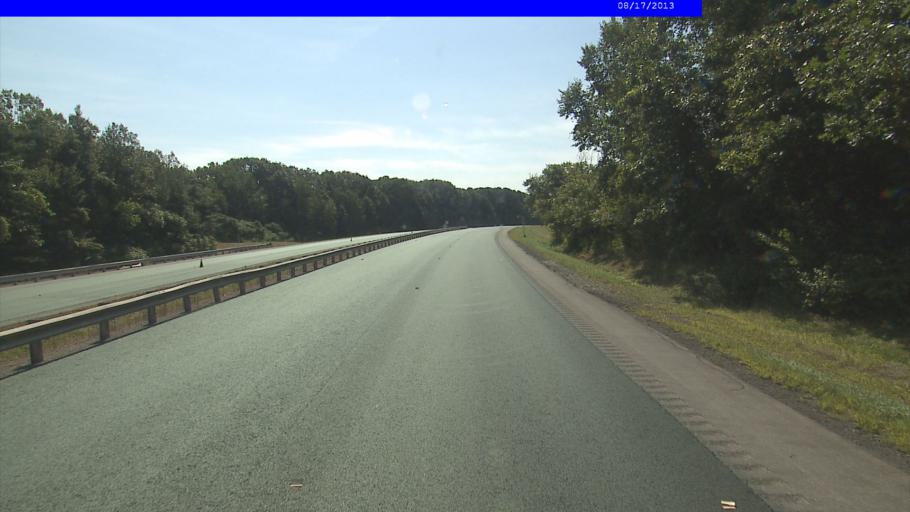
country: US
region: New Hampshire
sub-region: Cheshire County
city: Chesterfield
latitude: 42.9437
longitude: -72.5297
